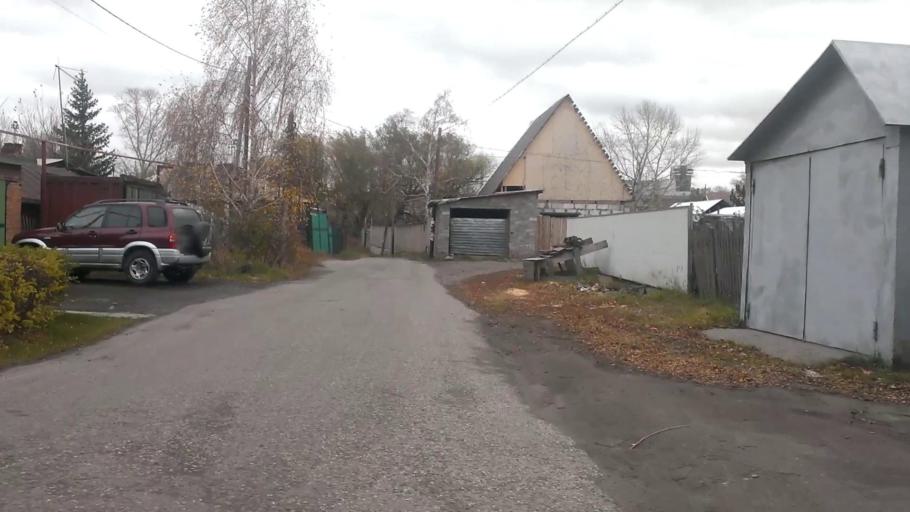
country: RU
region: Altai Krai
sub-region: Gorod Barnaulskiy
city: Barnaul
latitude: 53.3511
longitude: 83.7487
